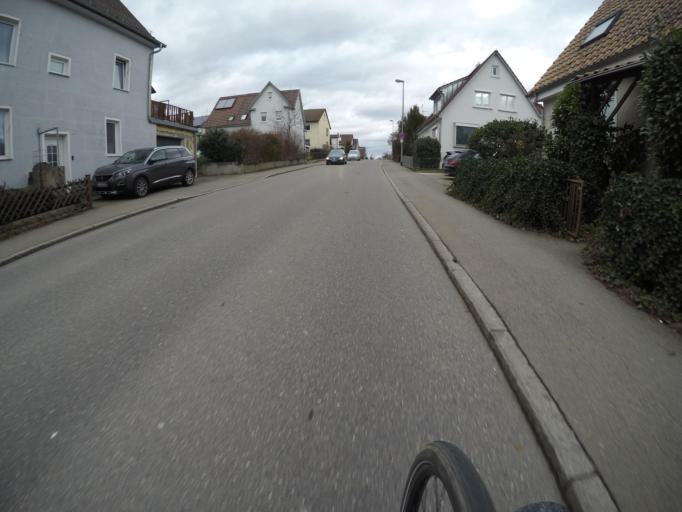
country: DE
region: Baden-Wuerttemberg
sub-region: Tuebingen Region
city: Reutlingen
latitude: 48.5018
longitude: 9.1800
